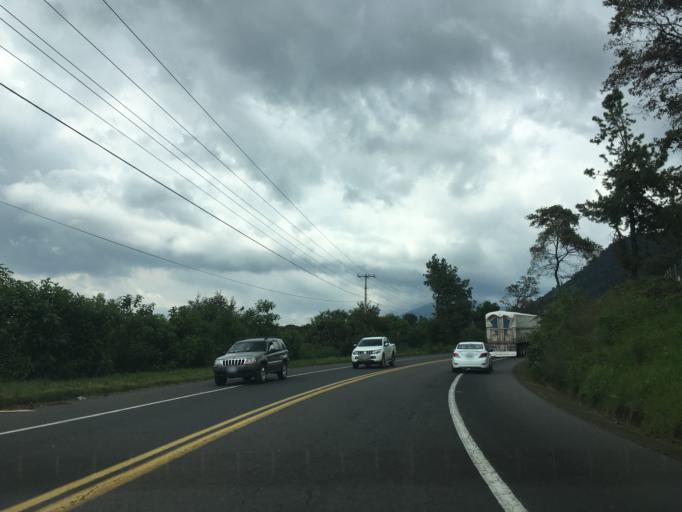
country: MX
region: Michoacan
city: Capacuaro
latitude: 19.5128
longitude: -102.0781
